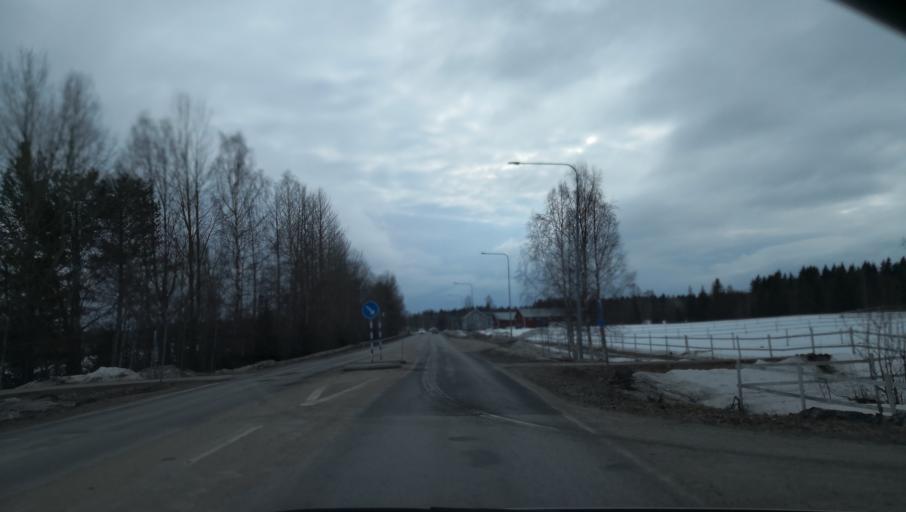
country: SE
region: Vaesterbotten
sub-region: Vannas Kommun
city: Vaennaes
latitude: 63.9175
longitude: 19.7775
